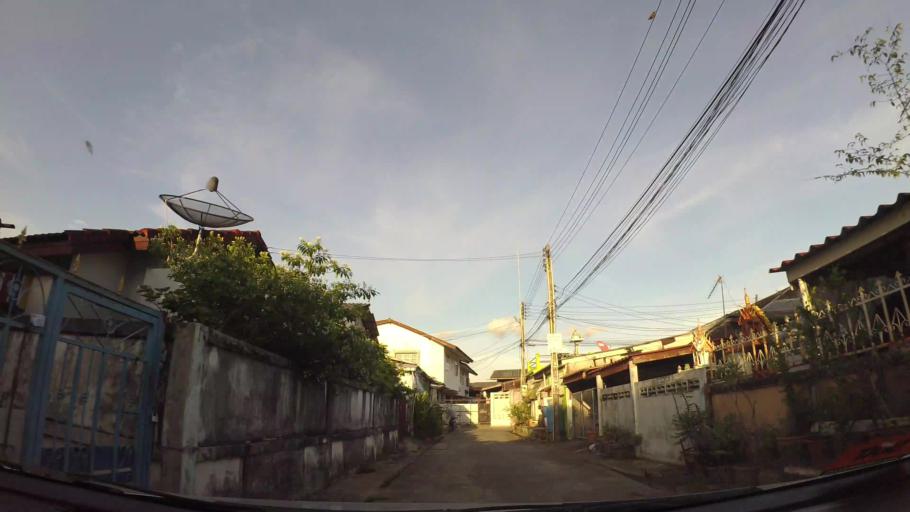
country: TH
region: Rayong
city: Rayong
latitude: 12.6873
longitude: 101.2780
